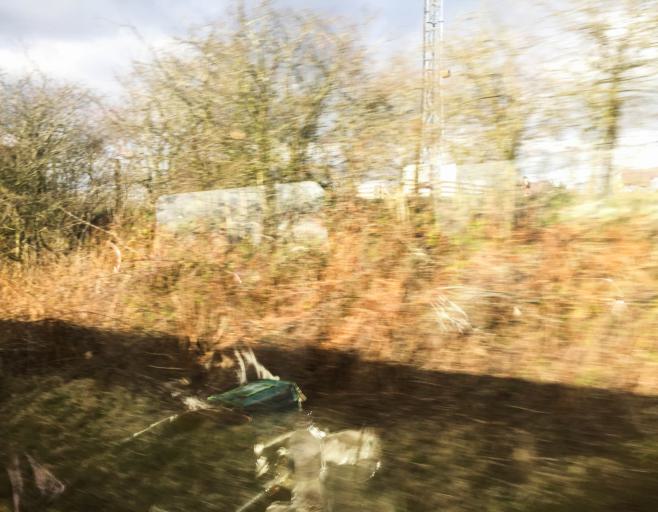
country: GB
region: Scotland
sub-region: South Lanarkshire
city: Carluke
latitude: 55.7099
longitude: -3.8272
